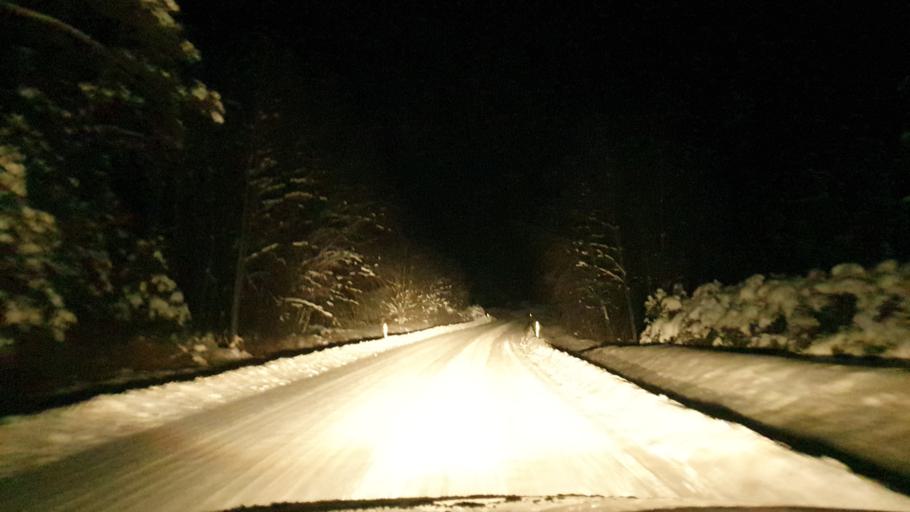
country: EE
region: Vorumaa
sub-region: Antsla vald
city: Vana-Antsla
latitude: 57.9599
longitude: 26.6623
